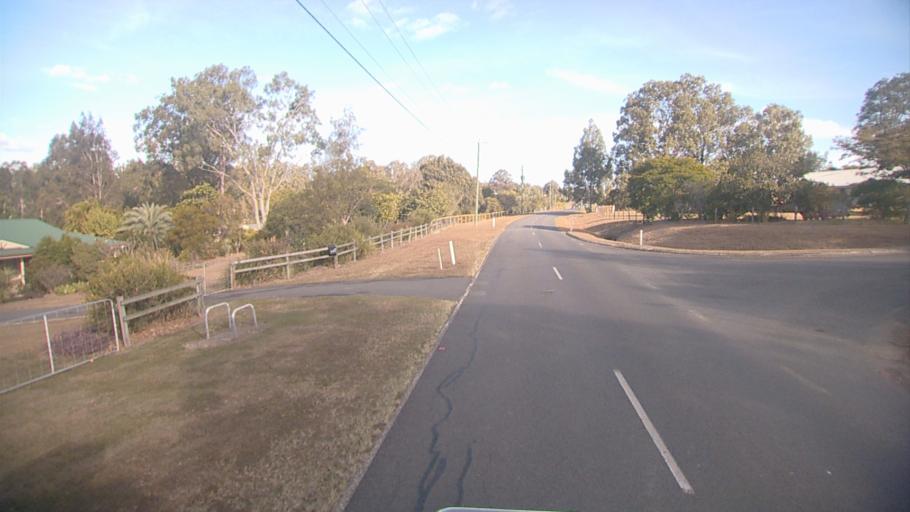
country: AU
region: Queensland
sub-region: Logan
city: Cedar Vale
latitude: -27.8722
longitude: 153.0039
